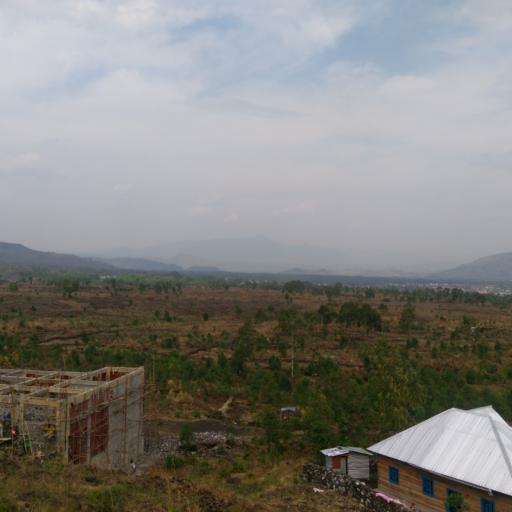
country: CD
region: Nord Kivu
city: Goma
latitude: -1.6310
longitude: 29.2240
